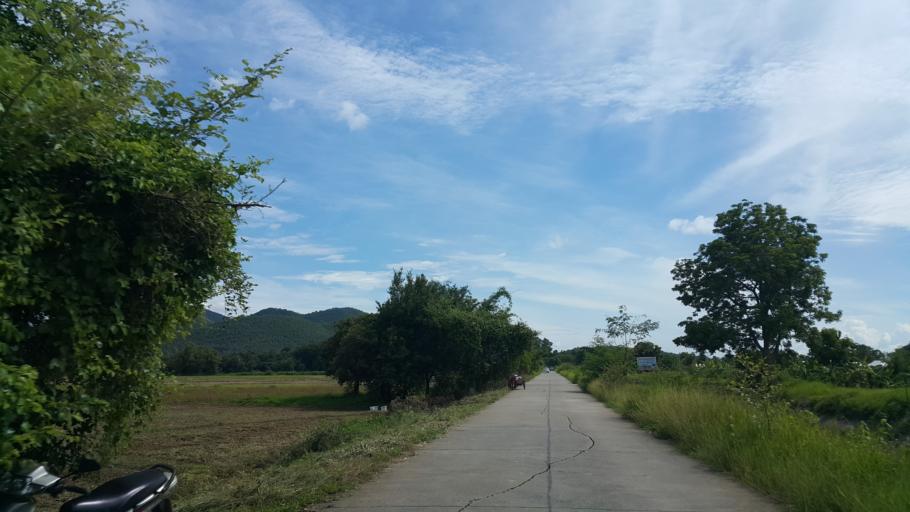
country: TH
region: Chiang Mai
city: Mae On
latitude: 18.7326
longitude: 99.1996
